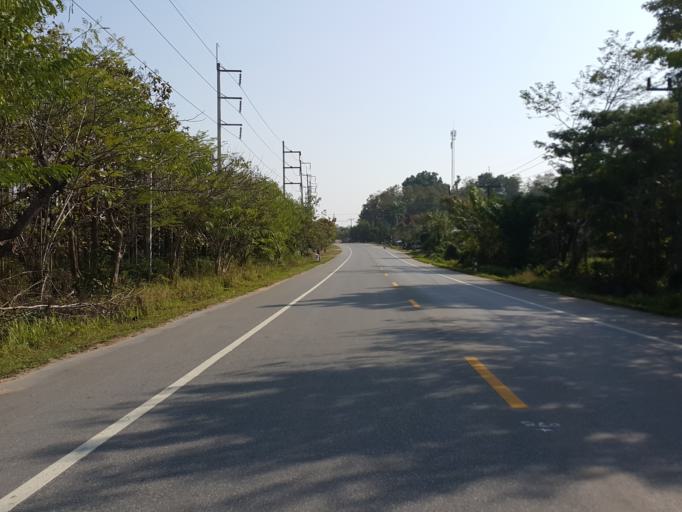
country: TH
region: Lampang
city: Chae Hom
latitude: 18.6490
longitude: 99.5374
